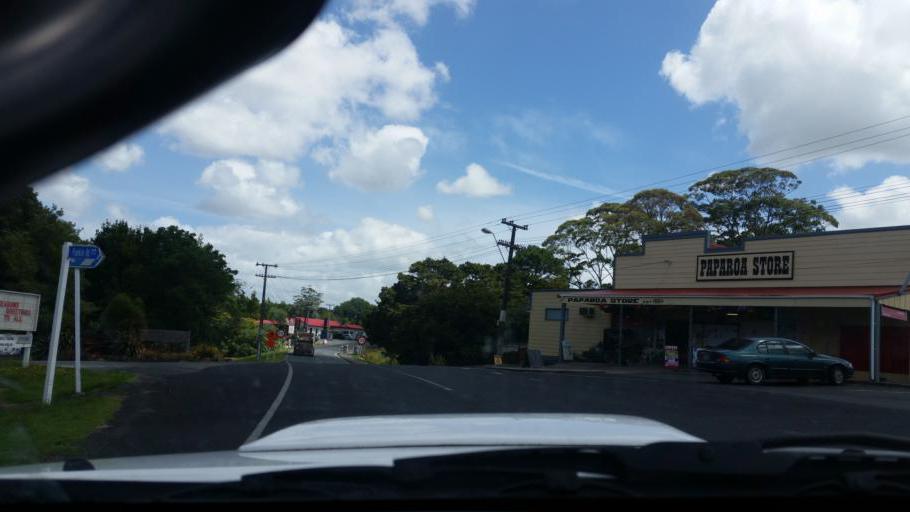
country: NZ
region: Northland
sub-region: Whangarei
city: Ruakaka
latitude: -36.1010
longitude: 174.2335
